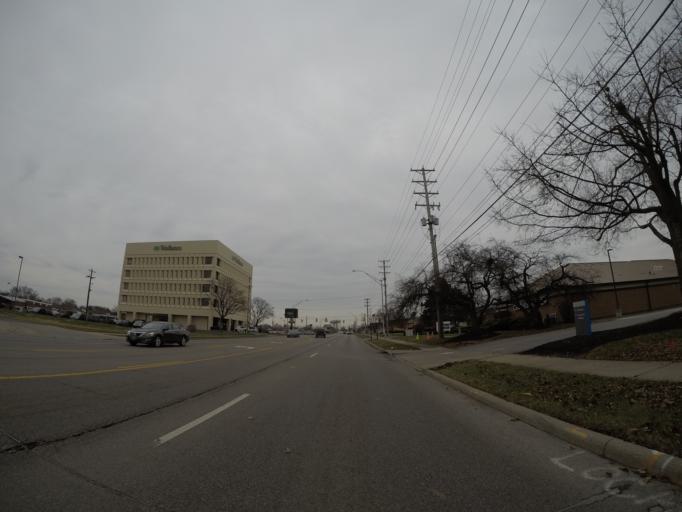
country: US
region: Ohio
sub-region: Franklin County
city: Dublin
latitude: 40.0564
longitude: -83.0733
